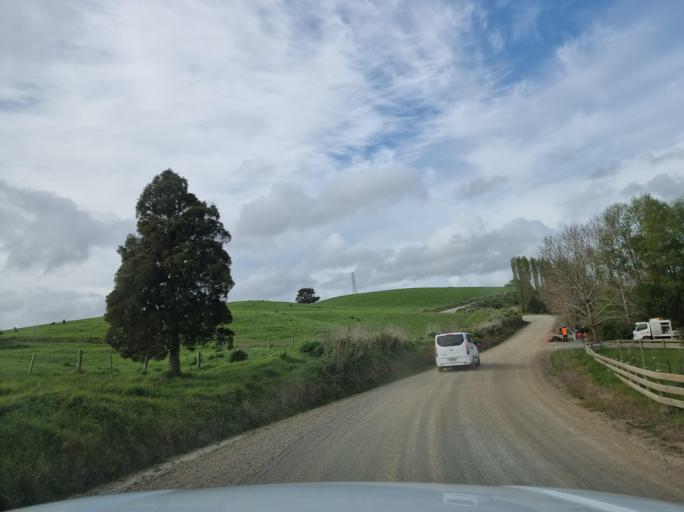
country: NZ
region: Northland
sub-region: Whangarei
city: Ruakaka
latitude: -36.0872
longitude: 174.3676
